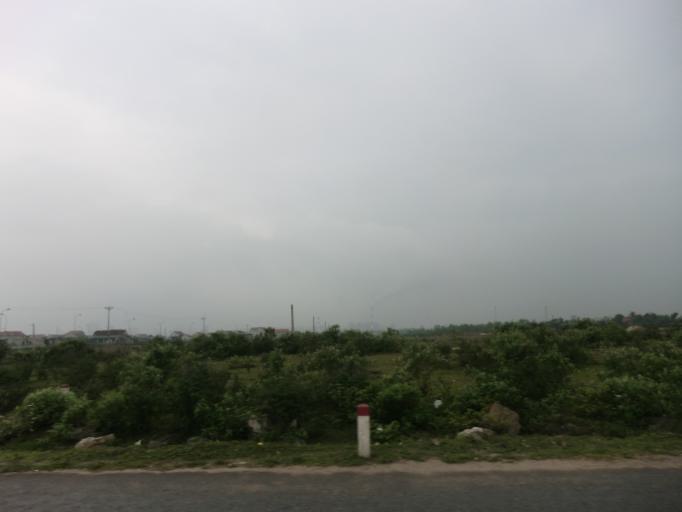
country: VN
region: Ha Tinh
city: Ky Anh
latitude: 18.0018
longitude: 106.4426
